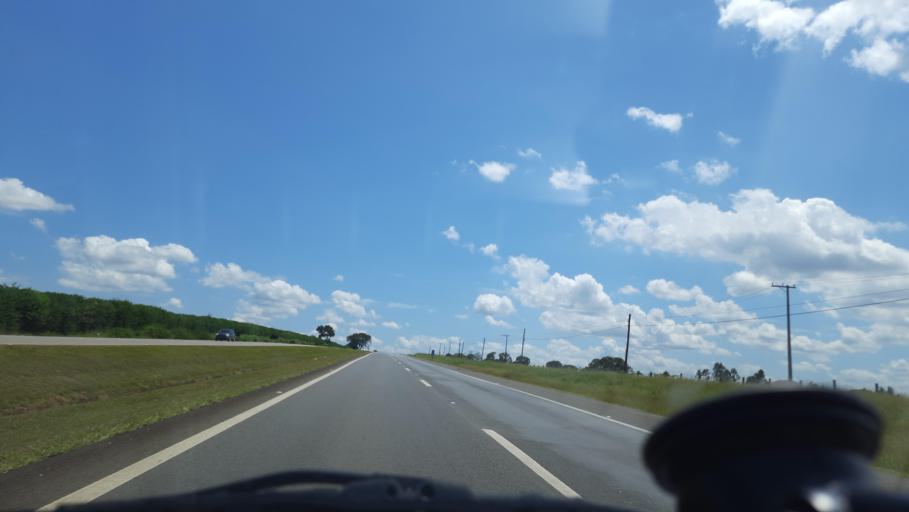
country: BR
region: Sao Paulo
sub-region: Moji-Guacu
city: Mogi-Gaucu
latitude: -22.2601
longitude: -46.9761
